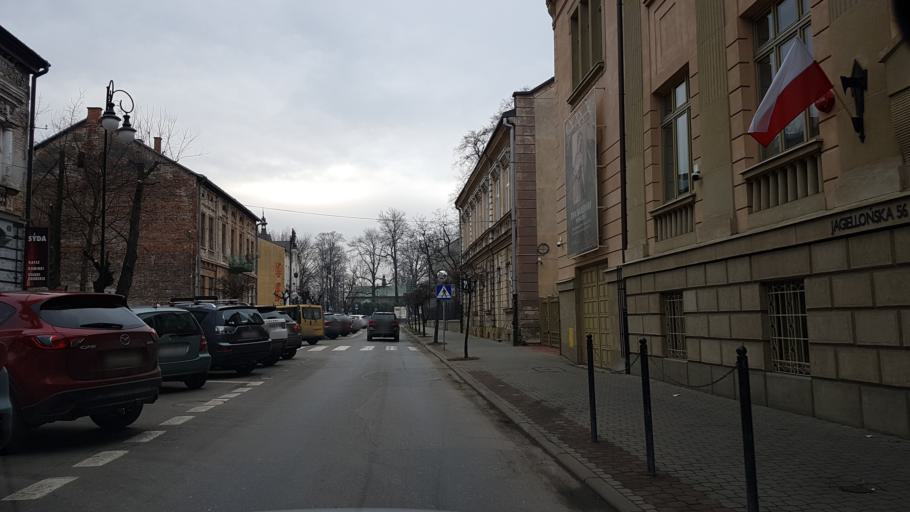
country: PL
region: Lesser Poland Voivodeship
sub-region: Powiat nowosadecki
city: Nowy Sacz
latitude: 49.6178
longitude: 20.6950
